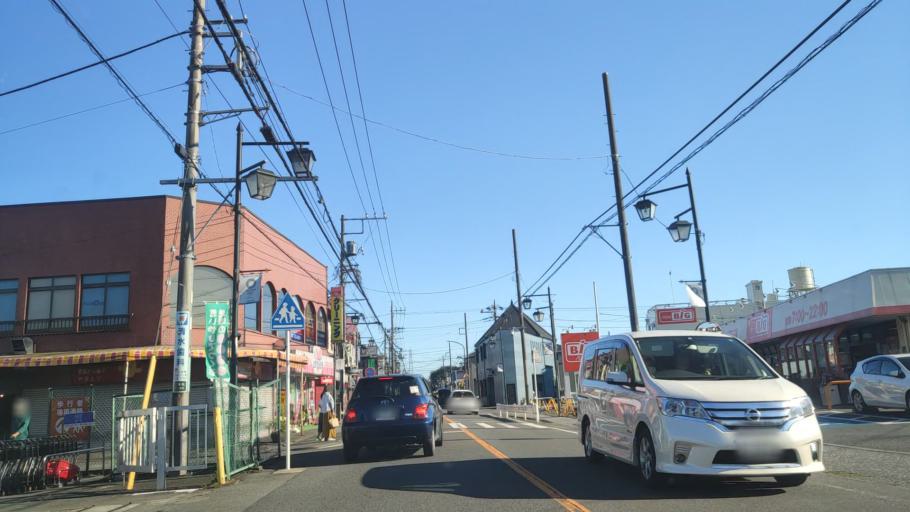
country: JP
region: Tokyo
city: Hachioji
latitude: 35.5963
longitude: 139.3208
